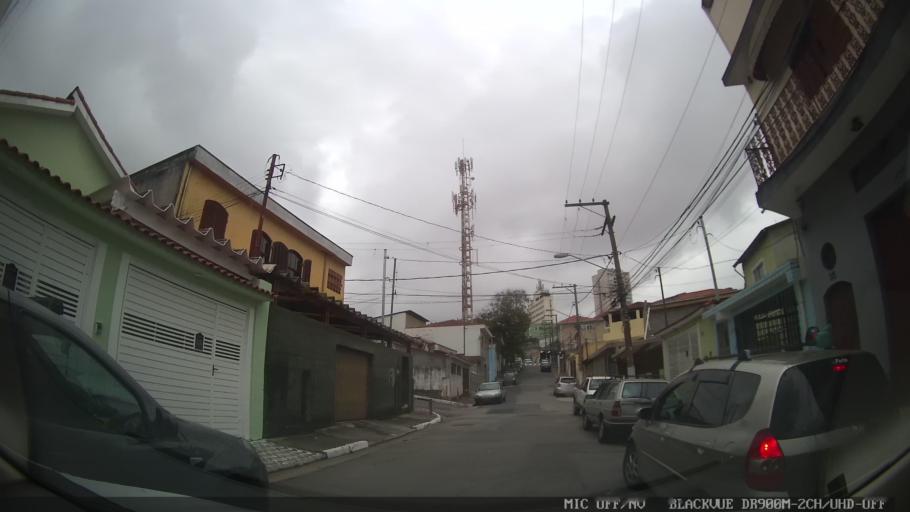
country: BR
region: Sao Paulo
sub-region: Sao Paulo
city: Sao Paulo
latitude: -23.4959
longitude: -46.5991
